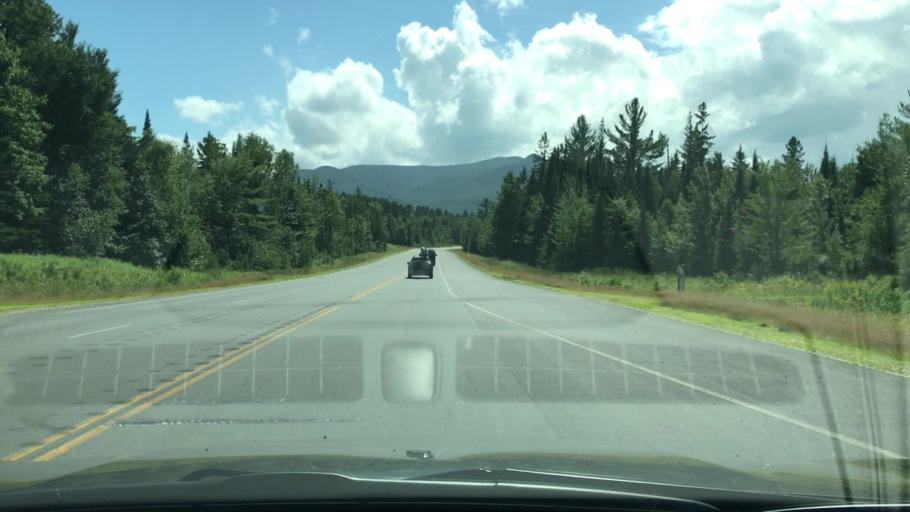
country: US
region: New Hampshire
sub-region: Coos County
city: Jefferson
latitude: 44.3728
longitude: -71.4410
